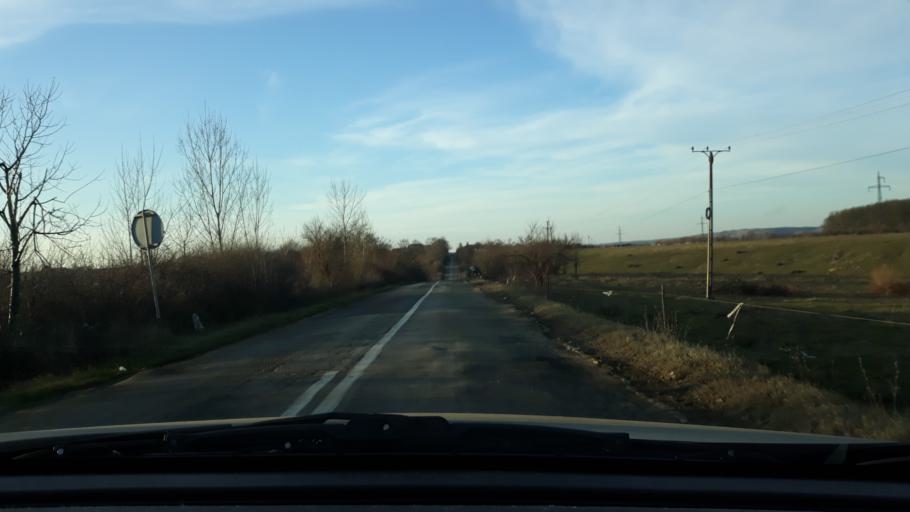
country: RO
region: Bihor
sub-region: Comuna Suplacu de Barcau
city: Suplacu de Barcau
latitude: 47.2700
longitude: 22.4960
